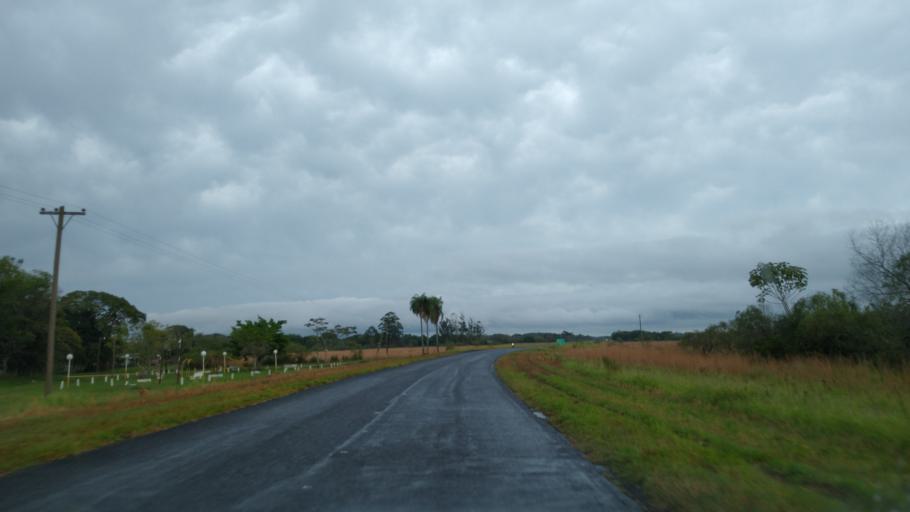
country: AR
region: Corrientes
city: Loreto
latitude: -27.7663
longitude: -57.2676
